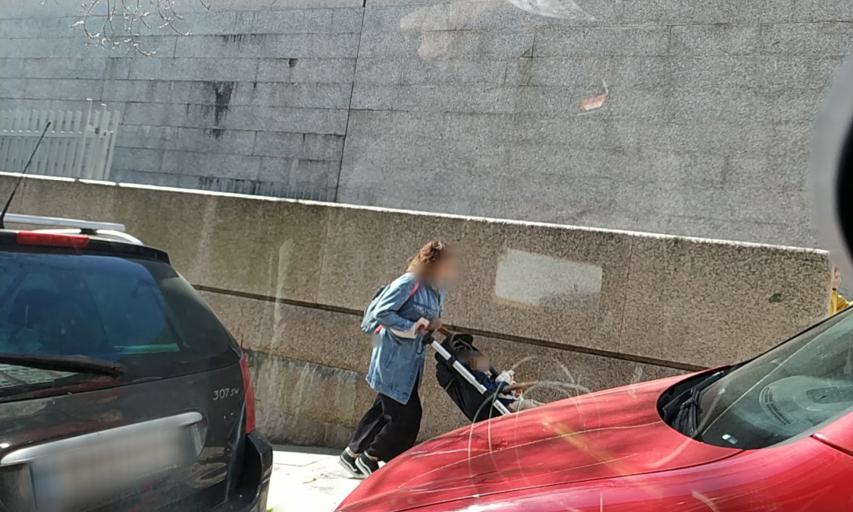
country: ES
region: Galicia
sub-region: Provincia da Coruna
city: A Coruna
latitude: 43.3775
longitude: -8.4058
